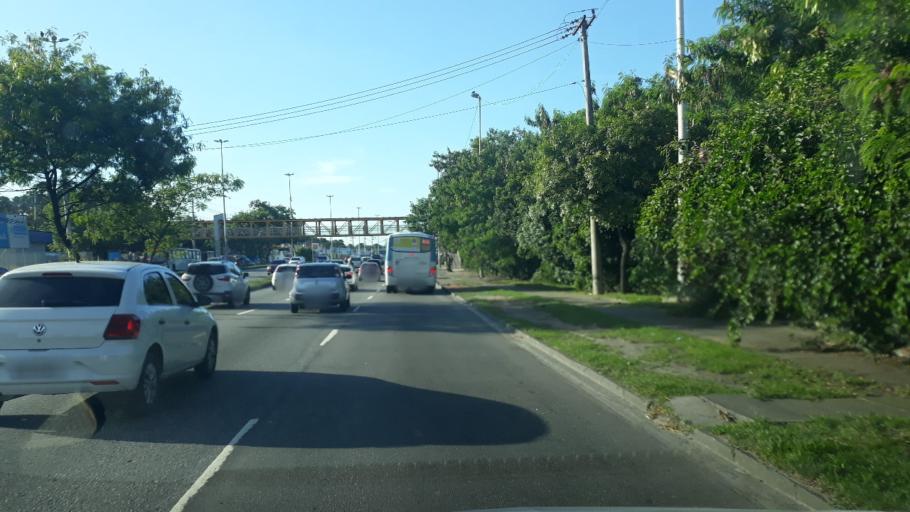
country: BR
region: Rio de Janeiro
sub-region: Sao Joao De Meriti
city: Sao Joao de Meriti
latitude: -22.9614
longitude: -43.3574
